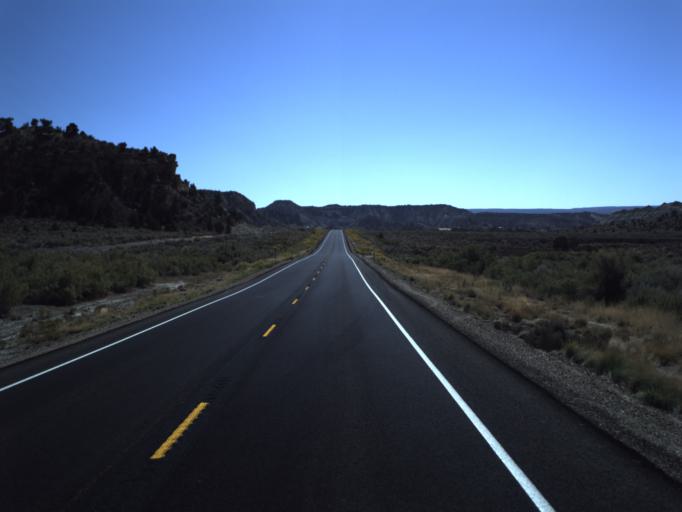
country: US
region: Utah
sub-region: Garfield County
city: Panguitch
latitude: 37.5834
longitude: -111.9843
